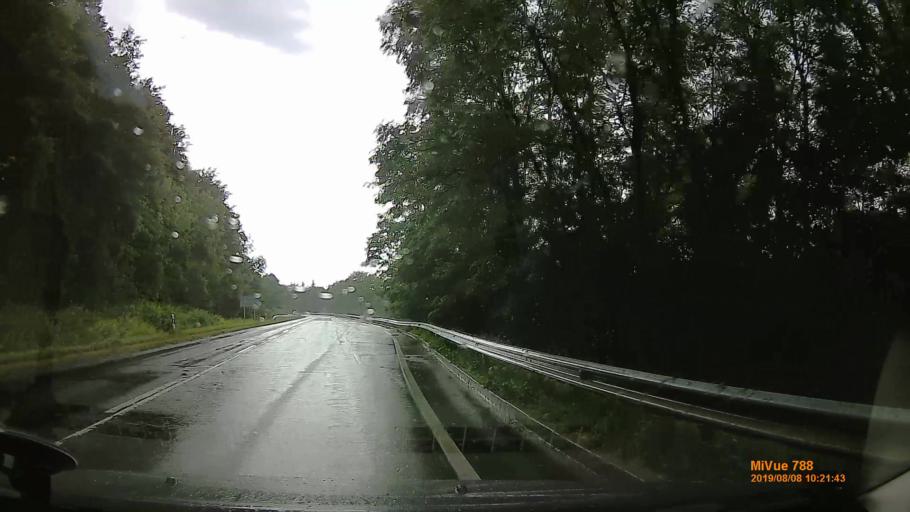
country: HU
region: Zala
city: Zalaegerszeg
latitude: 46.7346
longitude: 16.8560
